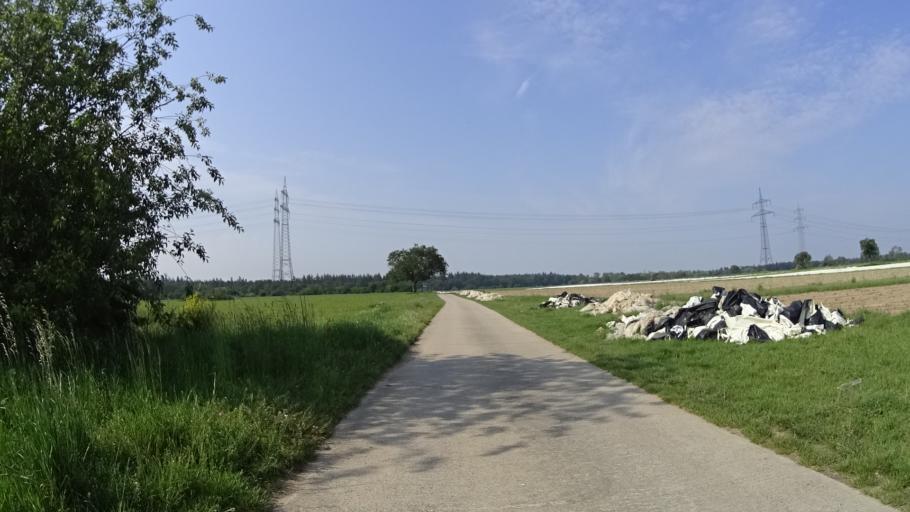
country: DE
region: Baden-Wuerttemberg
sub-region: Karlsruhe Region
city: Hambrucken
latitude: 49.2091
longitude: 8.5236
